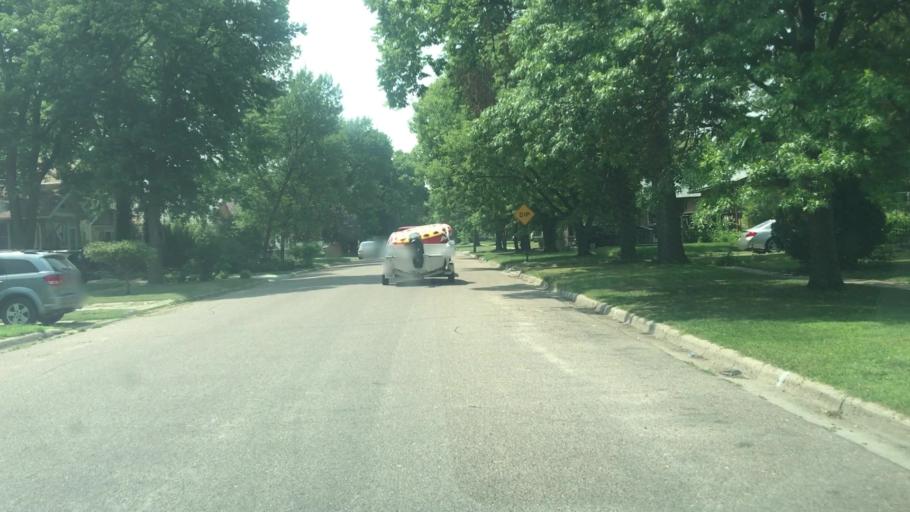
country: US
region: Nebraska
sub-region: Hall County
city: Grand Island
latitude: 40.9187
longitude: -98.3521
